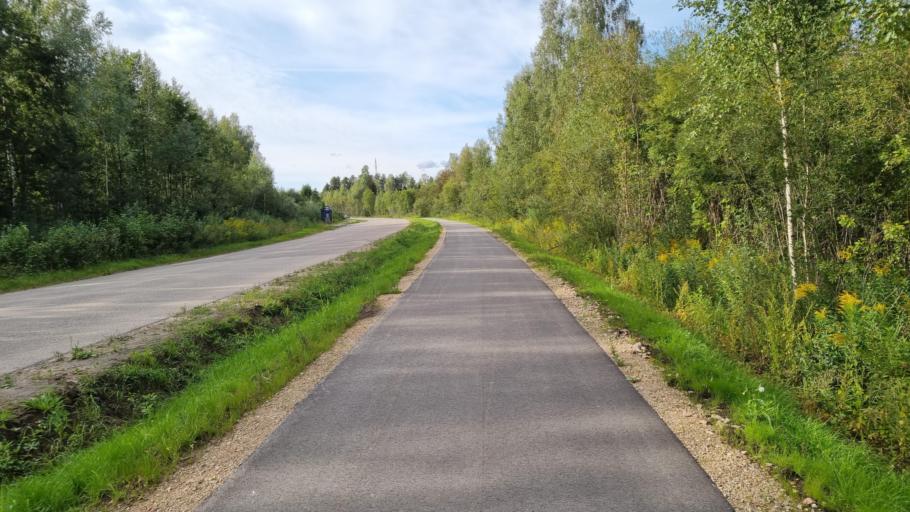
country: LV
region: Lecava
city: Iecava
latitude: 56.6964
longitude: 24.0854
